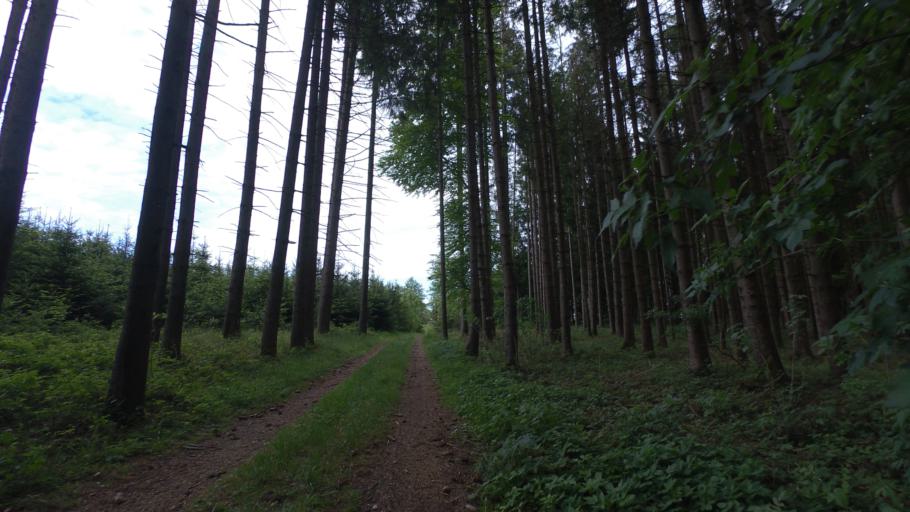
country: DE
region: Bavaria
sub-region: Upper Bavaria
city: Nussdorf
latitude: 47.9070
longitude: 12.6068
